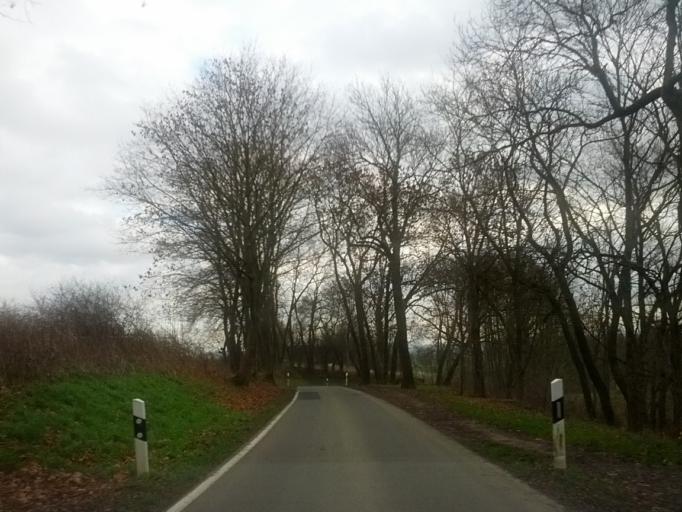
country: DE
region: Thuringia
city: Haina
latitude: 51.0250
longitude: 10.4682
